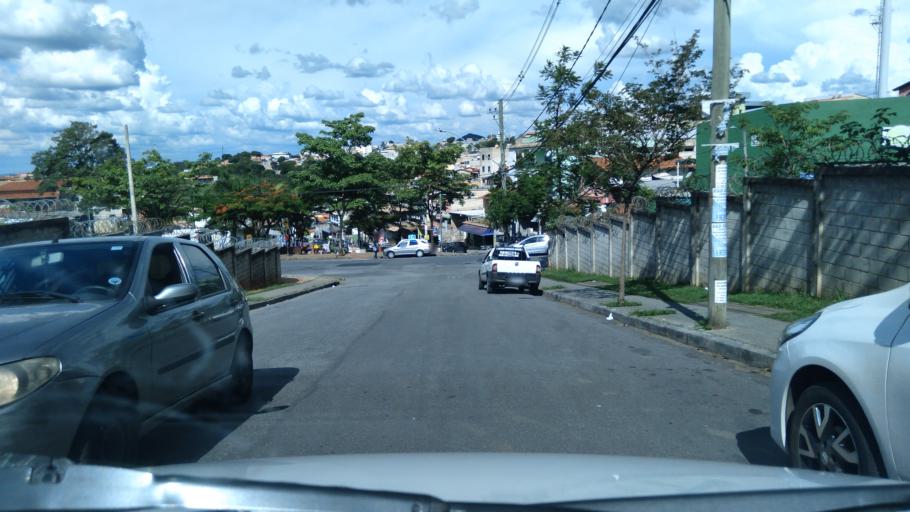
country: BR
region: Minas Gerais
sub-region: Belo Horizonte
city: Belo Horizonte
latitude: -19.8630
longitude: -43.8905
